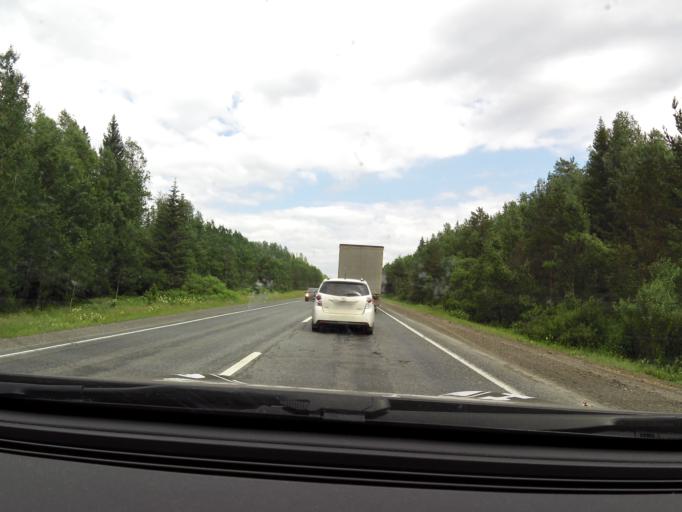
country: RU
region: Sverdlovsk
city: Nizhniye Sergi
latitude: 56.8236
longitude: 59.3047
